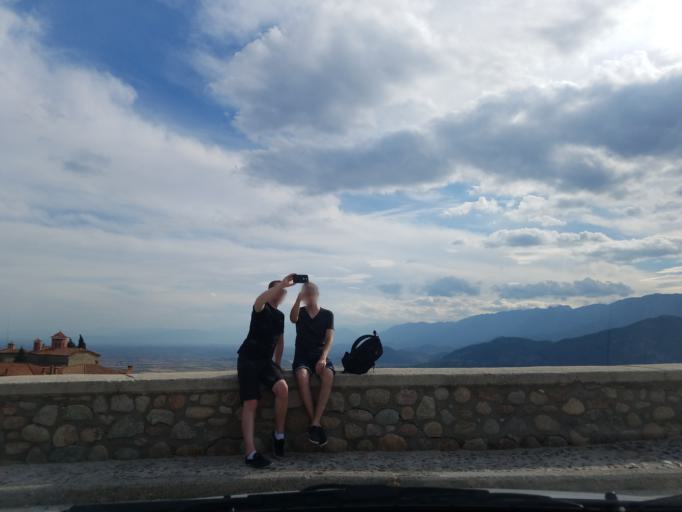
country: GR
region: Thessaly
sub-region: Trikala
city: Kalampaka
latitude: 39.7106
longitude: 21.6376
